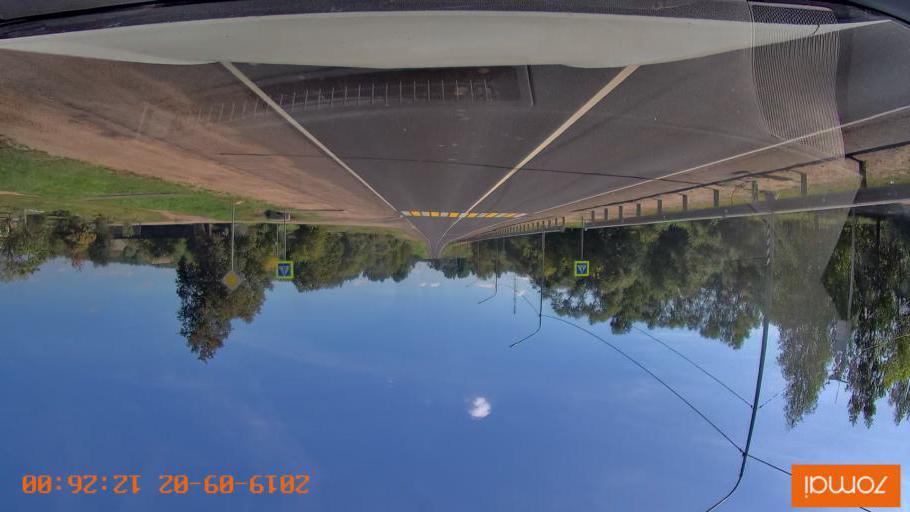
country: RU
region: Smolensk
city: Shumyachi
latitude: 53.8589
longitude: 32.5740
